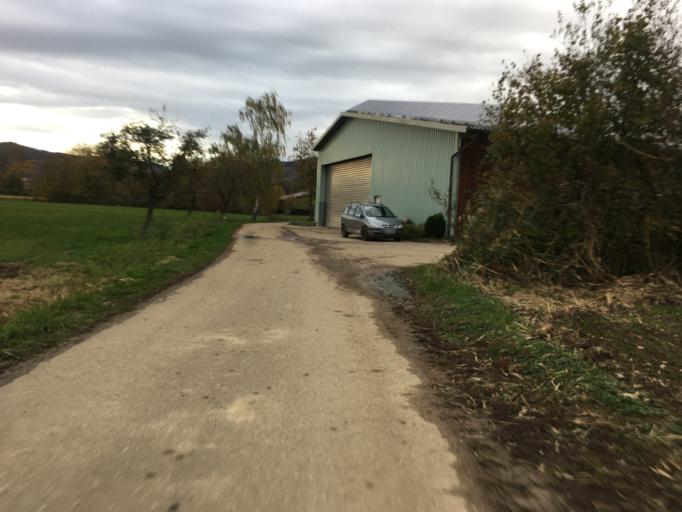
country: DE
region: Baden-Wuerttemberg
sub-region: Freiburg Region
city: Botzingen
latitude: 48.0705
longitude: 7.7331
